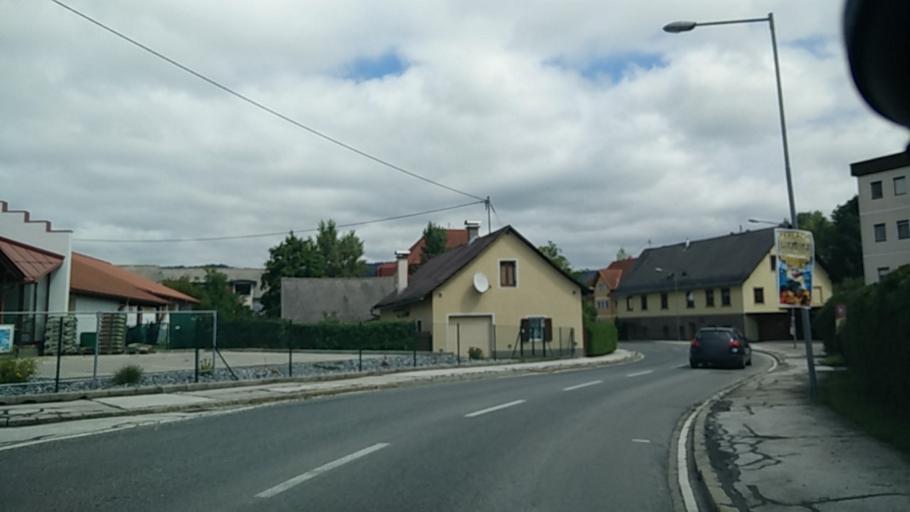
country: AT
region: Carinthia
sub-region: Politischer Bezirk Klagenfurt Land
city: Ferlach
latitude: 46.5291
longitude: 14.3011
